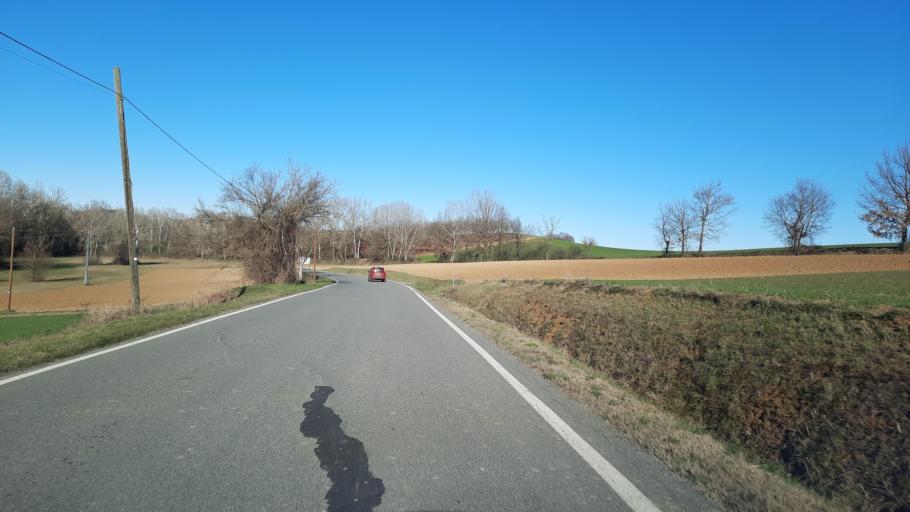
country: IT
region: Piedmont
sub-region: Provincia di Alessandria
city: Frassinello Monferrato
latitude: 45.0452
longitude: 8.3893
